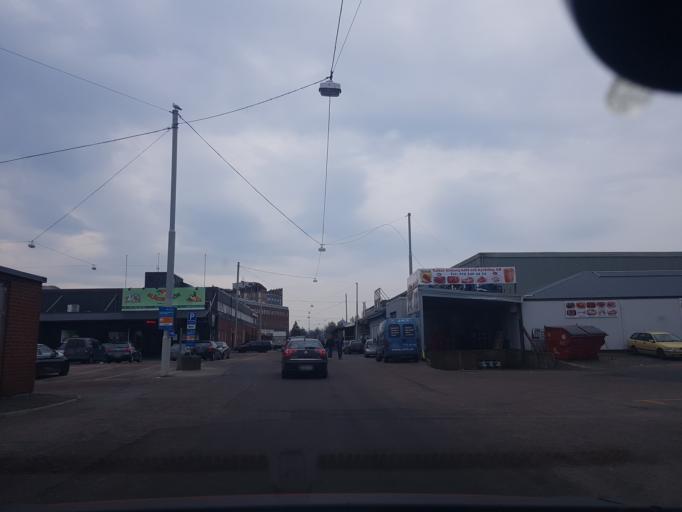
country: SE
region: Vaestra Goetaland
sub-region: Goteborg
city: Goeteborg
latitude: 57.7217
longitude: 11.9988
